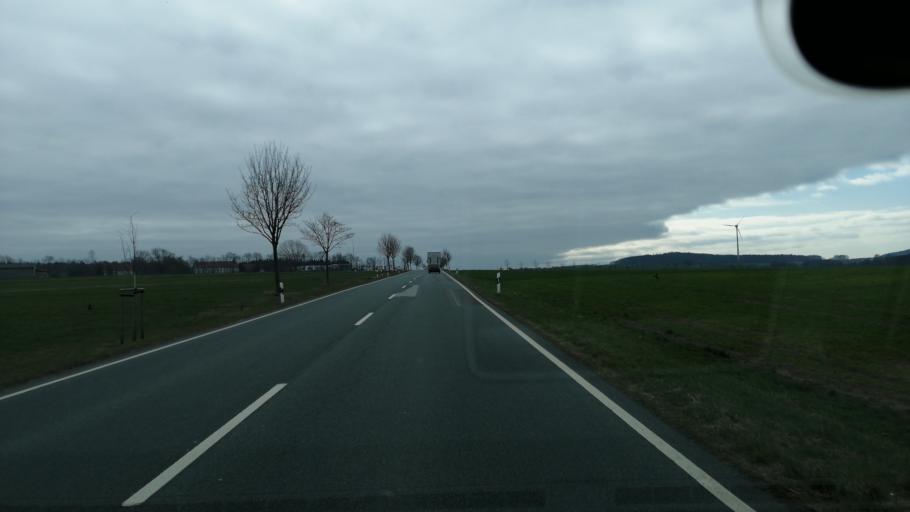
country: DE
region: Saxony
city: Lobau
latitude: 51.0797
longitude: 14.6751
